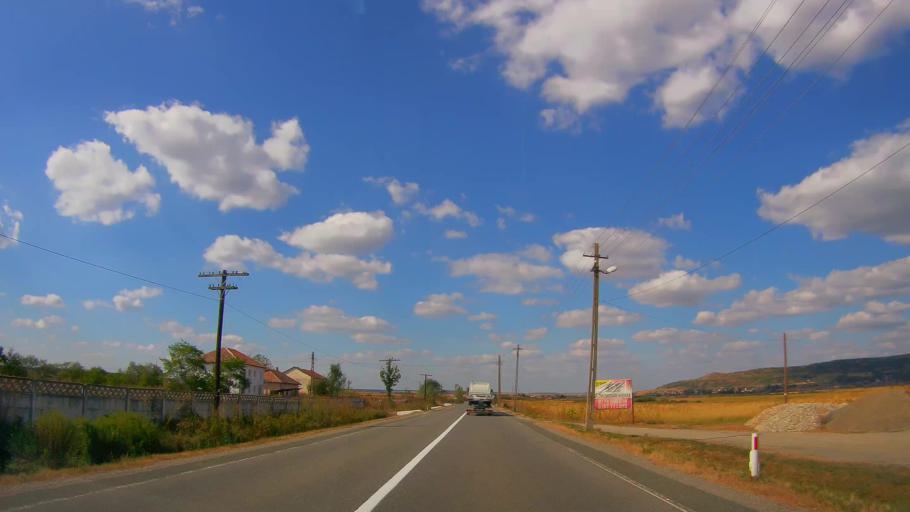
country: RO
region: Salaj
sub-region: Comuna Bobota
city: Dersida
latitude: 47.3653
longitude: 22.7921
